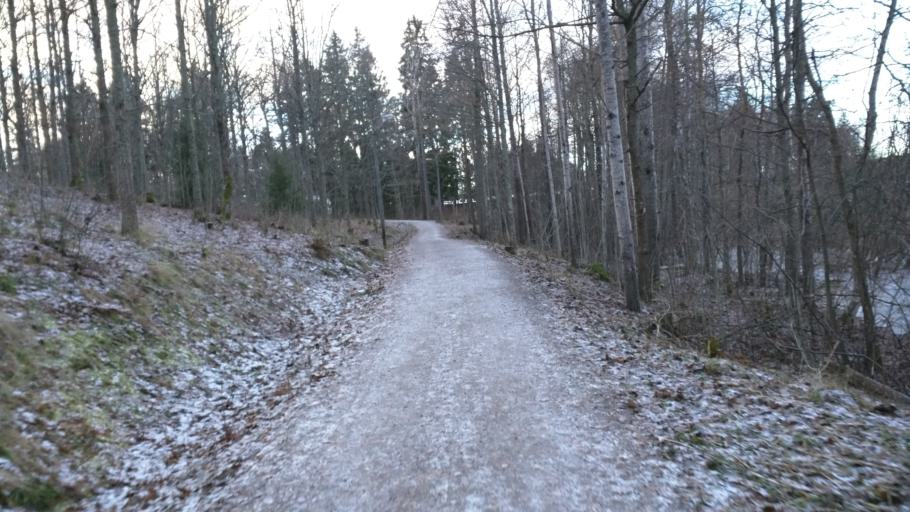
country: FI
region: Uusimaa
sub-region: Helsinki
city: Kauniainen
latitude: 60.2460
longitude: 24.7394
